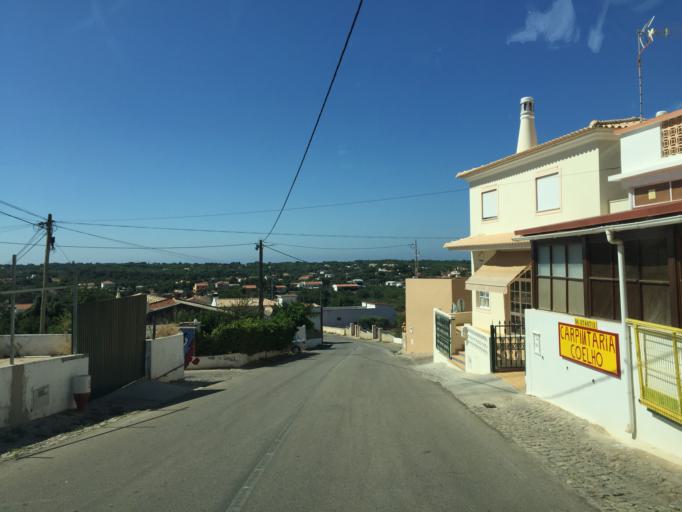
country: PT
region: Faro
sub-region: Loule
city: Vilamoura
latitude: 37.1160
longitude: -8.0988
